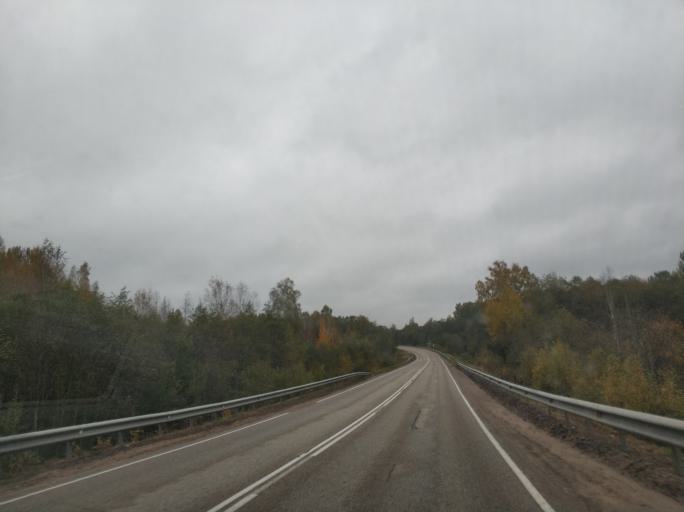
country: BY
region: Vitebsk
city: Rasony
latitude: 56.0587
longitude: 28.7143
